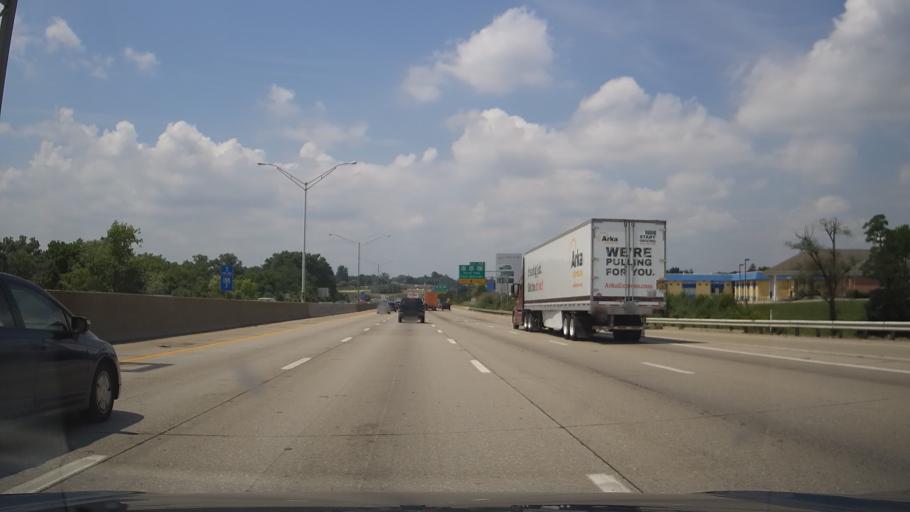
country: US
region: Kentucky
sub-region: Kenton County
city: Fort Mitchell
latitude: 39.0570
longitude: -84.5419
